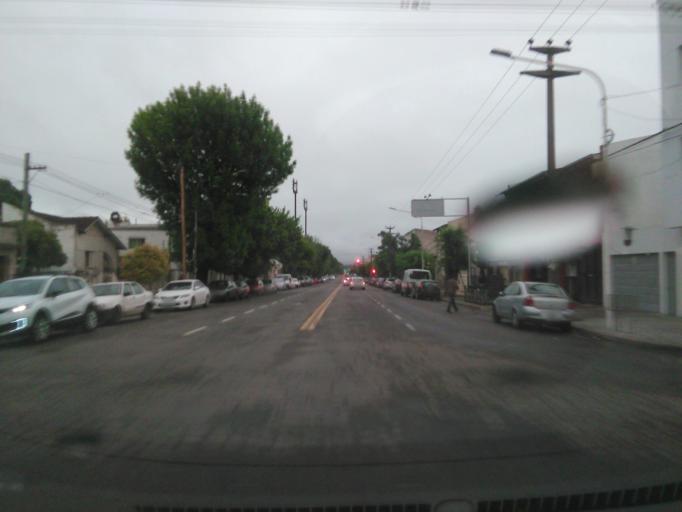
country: AR
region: Buenos Aires
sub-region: Partido de Tandil
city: Tandil
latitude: -37.3343
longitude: -59.1420
